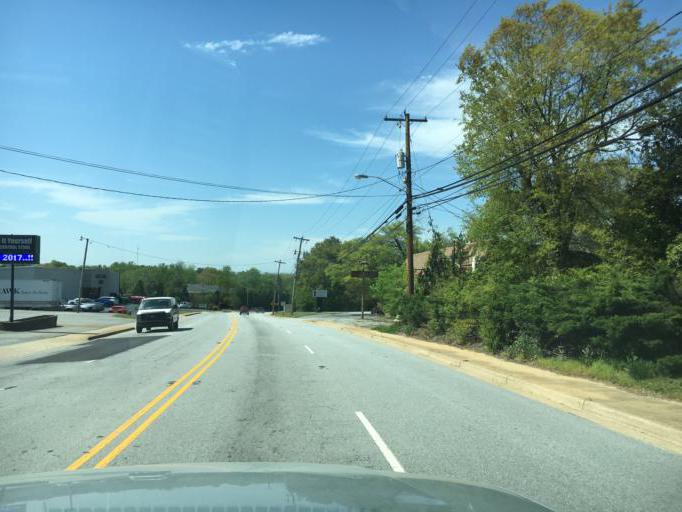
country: US
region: South Carolina
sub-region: Greenville County
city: Greer
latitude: 34.9531
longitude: -82.2270
